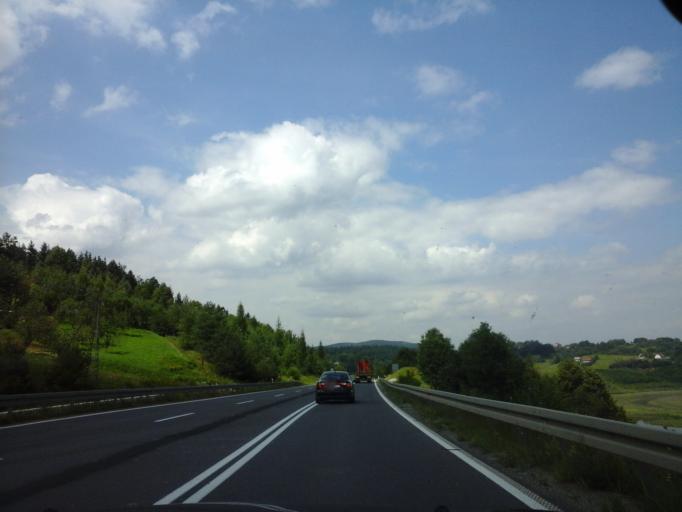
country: PL
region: Lesser Poland Voivodeship
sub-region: Powiat wadowicki
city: Jaroszowice
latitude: 49.8142
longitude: 19.5279
